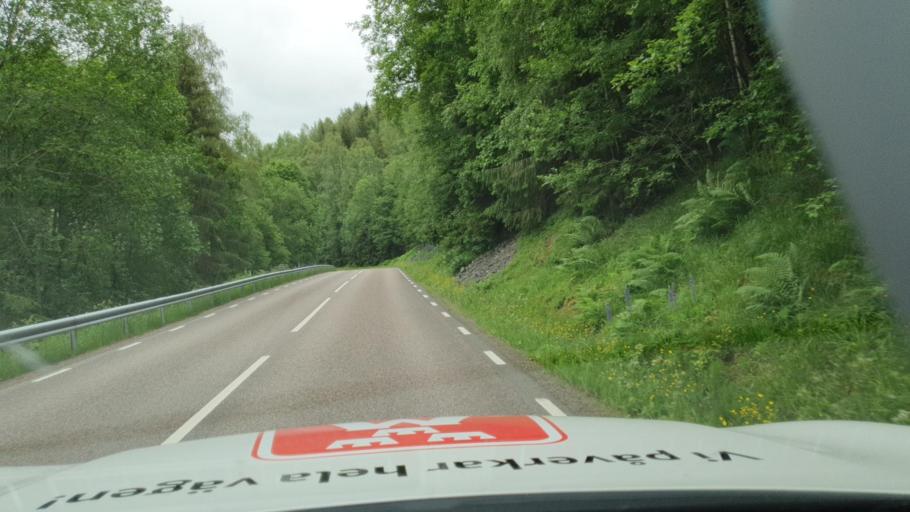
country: SE
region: Vaermland
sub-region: Sunne Kommun
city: Sunne
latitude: 59.8234
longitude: 12.9955
